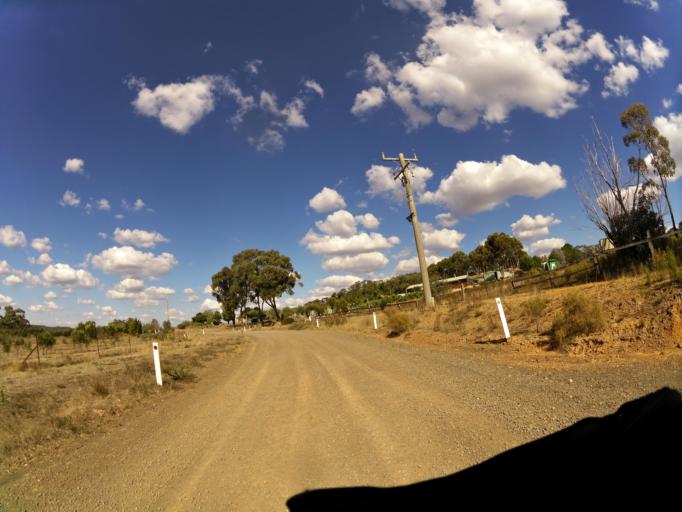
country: AU
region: Victoria
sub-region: Greater Bendigo
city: Kennington
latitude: -36.9554
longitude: 144.7770
